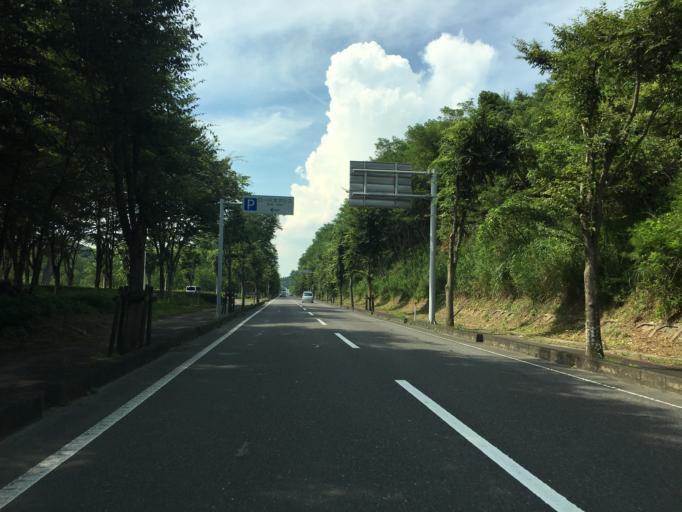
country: JP
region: Fukushima
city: Sukagawa
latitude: 37.2459
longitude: 140.4329
